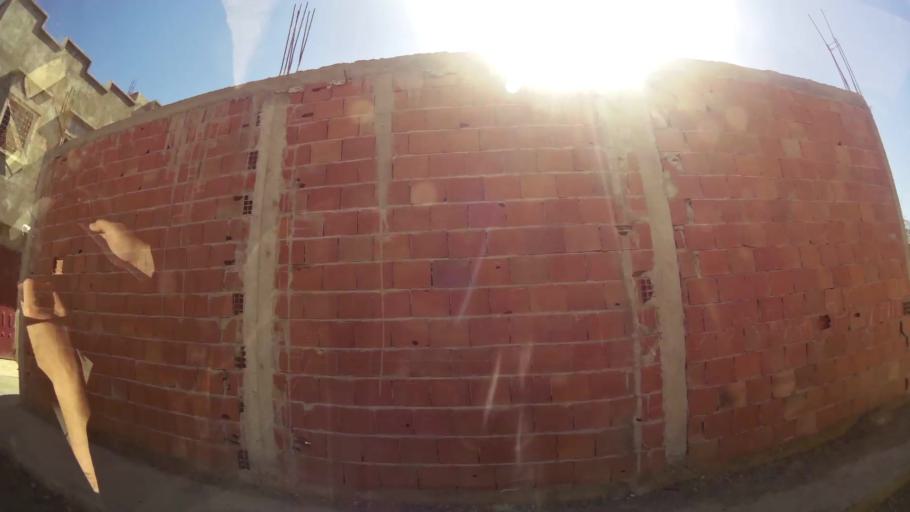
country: MA
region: Oriental
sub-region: Oujda-Angad
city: Oujda
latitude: 34.7229
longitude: -1.9021
